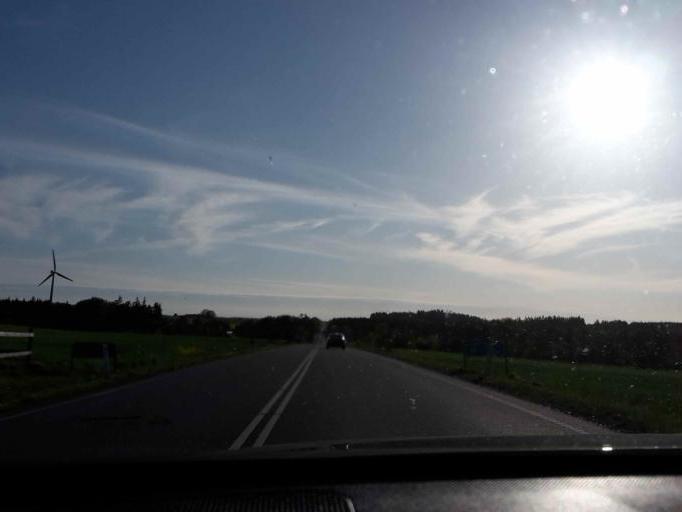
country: DK
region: Central Jutland
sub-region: Norddjurs Kommune
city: Allingabro
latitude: 56.4464
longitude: 10.2643
